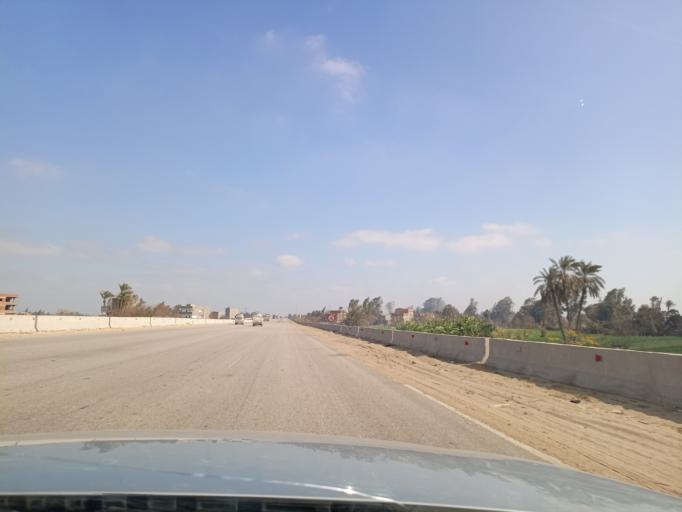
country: EG
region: Muhafazat al Minufiyah
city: Al Bajur
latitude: 30.4279
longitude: 31.0950
